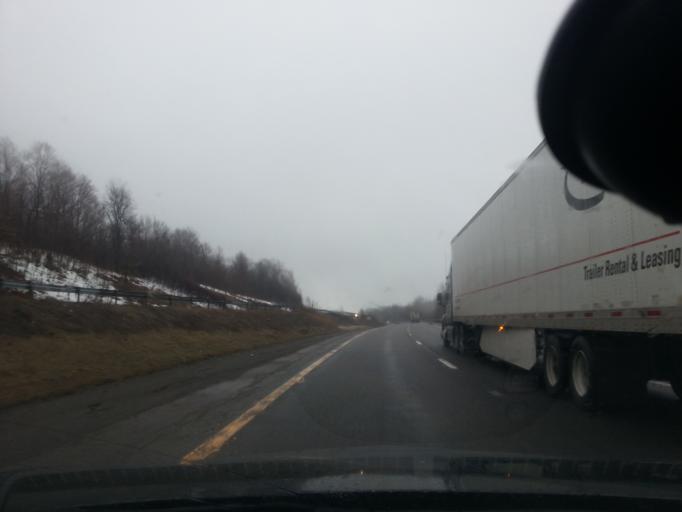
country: US
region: New York
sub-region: Onondaga County
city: Nedrow
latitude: 42.8383
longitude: -76.1232
